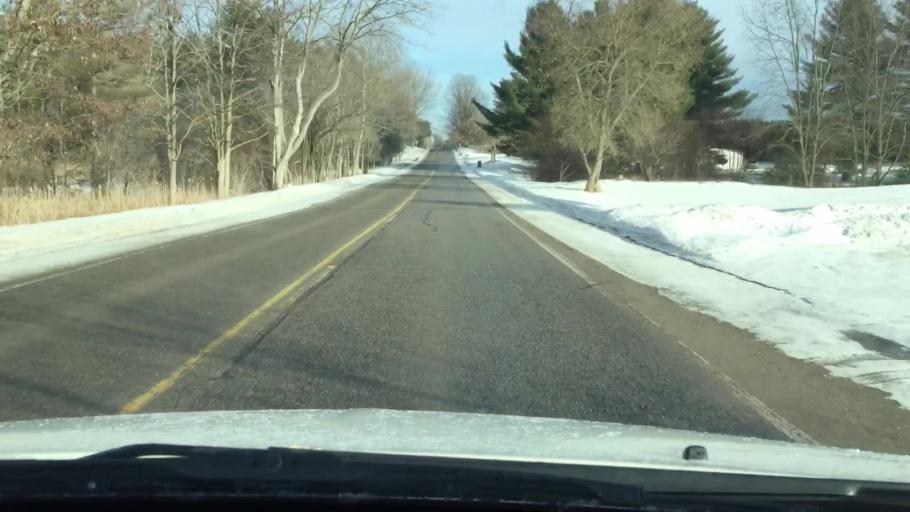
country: US
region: Michigan
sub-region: Kalkaska County
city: Kalkaska
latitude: 44.6412
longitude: -85.2693
